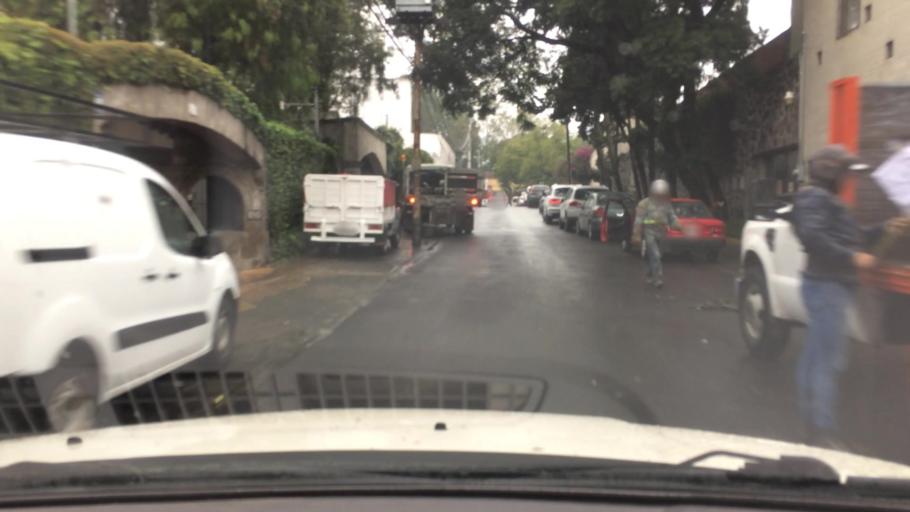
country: MX
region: Mexico City
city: Magdalena Contreras
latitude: 19.3157
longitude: -99.2113
